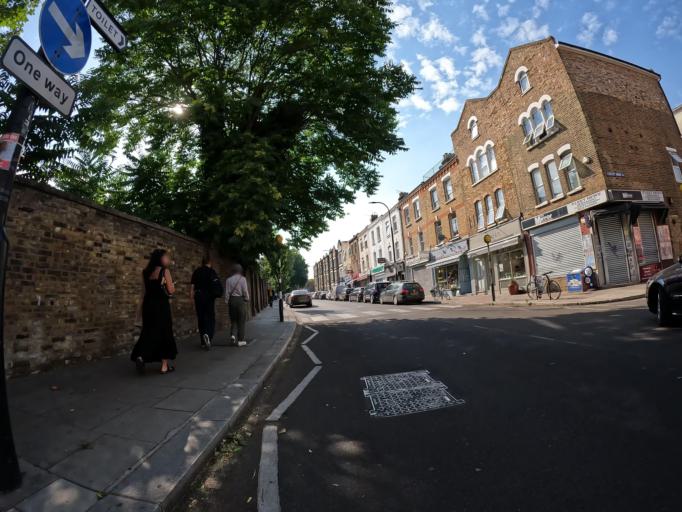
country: GB
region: England
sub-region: Greater London
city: Hendon
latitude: 51.5811
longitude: -0.2101
